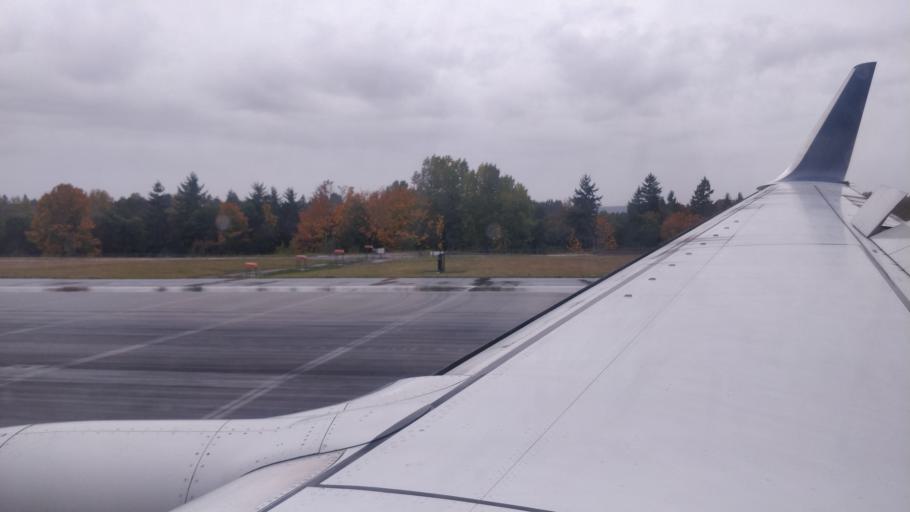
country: US
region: Washington
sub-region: King County
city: Normandy Park
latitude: 47.4443
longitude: -122.3176
